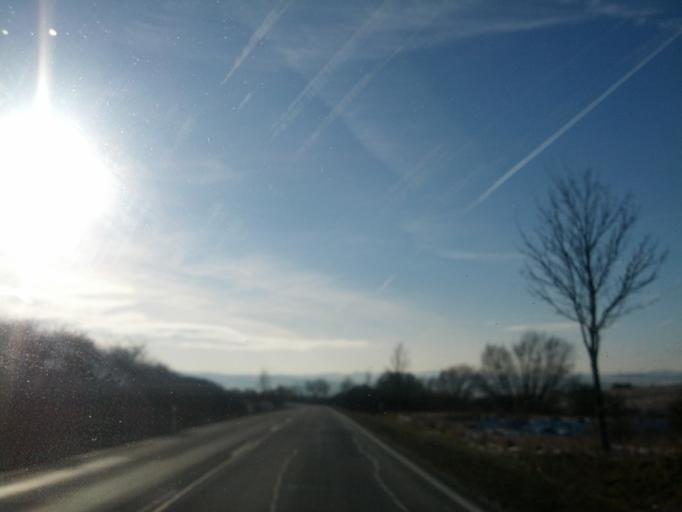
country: DE
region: Thuringia
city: Haina
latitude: 51.0073
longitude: 10.4480
